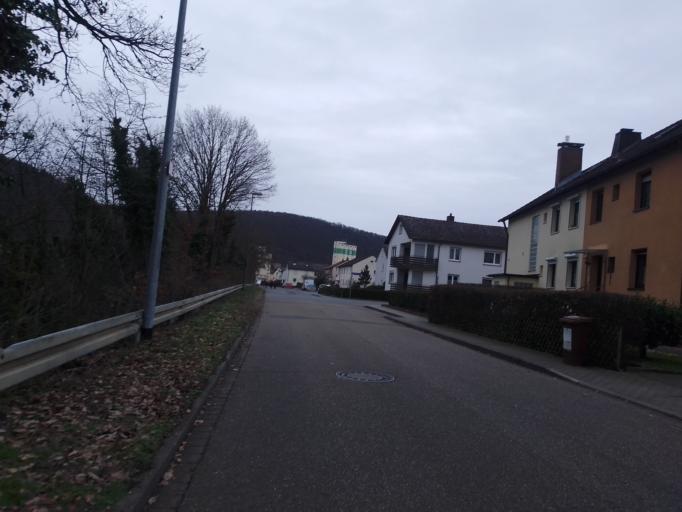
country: DE
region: Bavaria
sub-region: Regierungsbezirk Unterfranken
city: Hasloch
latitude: 49.7857
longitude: 9.4969
